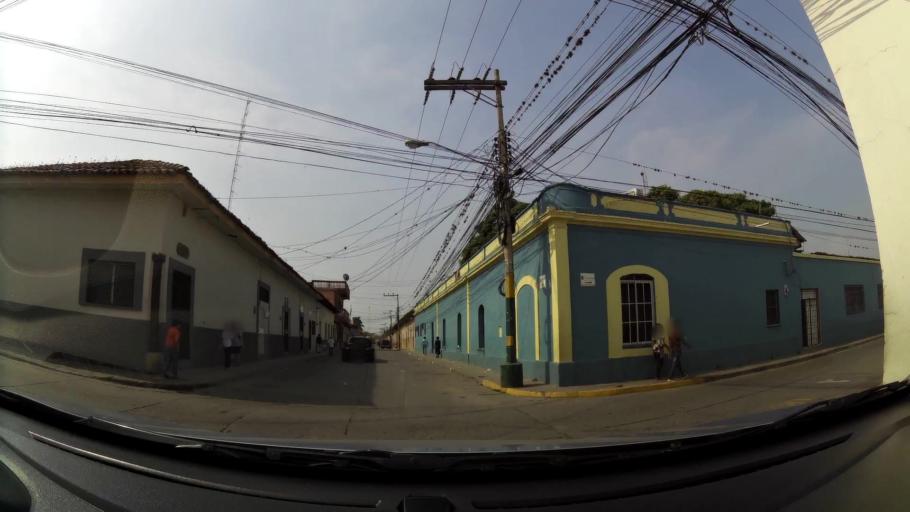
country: HN
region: Comayagua
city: Comayagua
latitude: 14.4593
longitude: -87.6402
